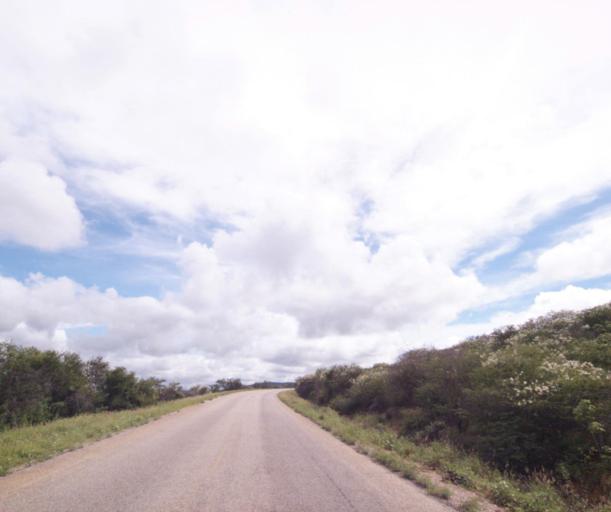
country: BR
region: Bahia
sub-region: Brumado
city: Brumado
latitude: -14.2024
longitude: -41.6184
